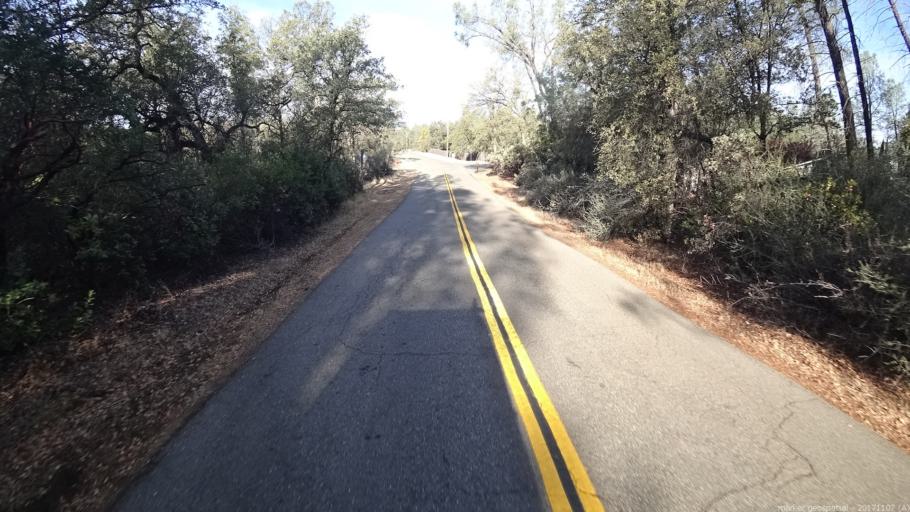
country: US
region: California
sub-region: Shasta County
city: Redding
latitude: 40.5503
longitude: -122.4409
